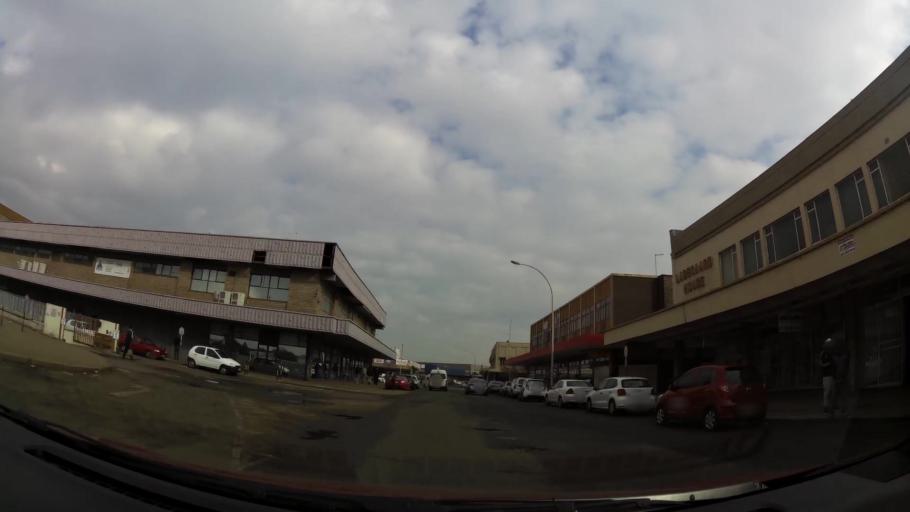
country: ZA
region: Gauteng
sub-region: Sedibeng District Municipality
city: Vanderbijlpark
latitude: -26.6965
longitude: 27.8362
